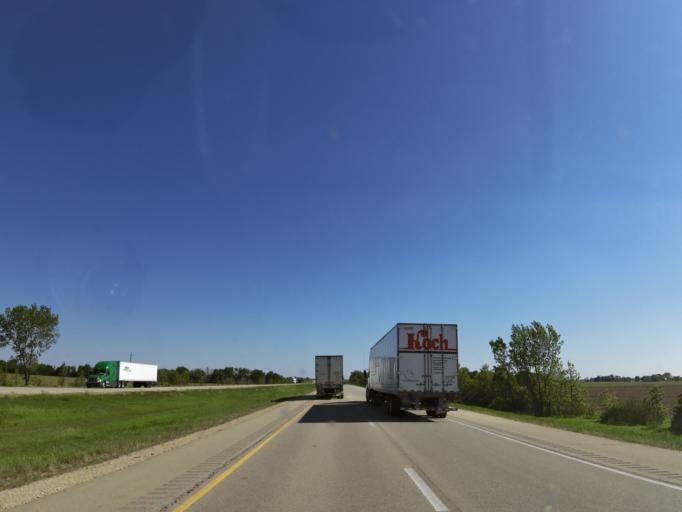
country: US
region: Illinois
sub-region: Ogle County
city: Rochelle
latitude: 41.7991
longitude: -89.0101
